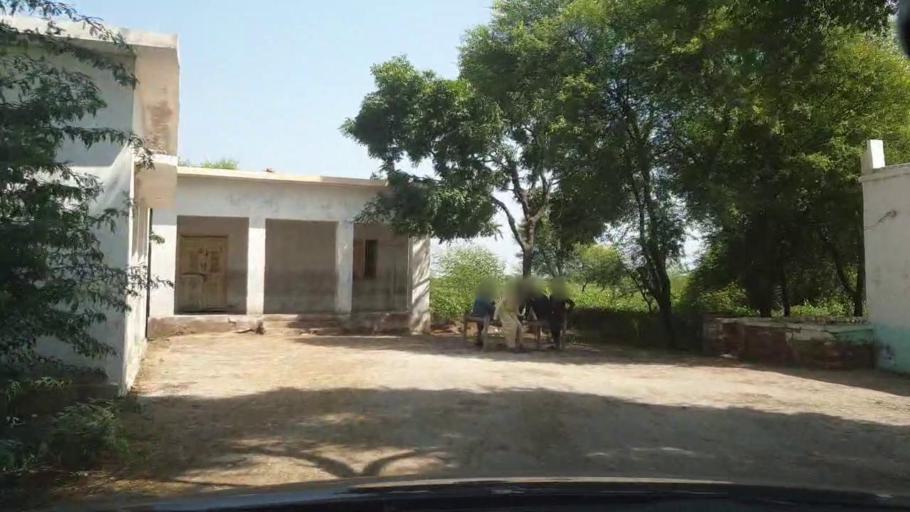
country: PK
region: Sindh
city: Naukot
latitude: 24.8031
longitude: 69.2180
